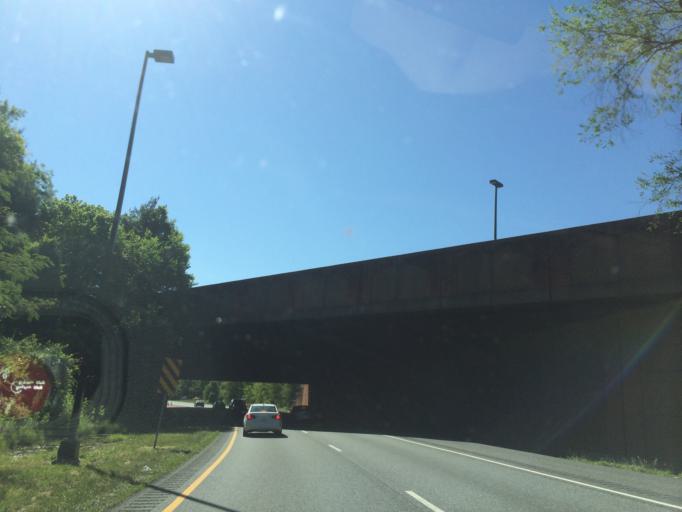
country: US
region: Maryland
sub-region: Anne Arundel County
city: Riva
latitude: 38.9851
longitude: -76.5761
